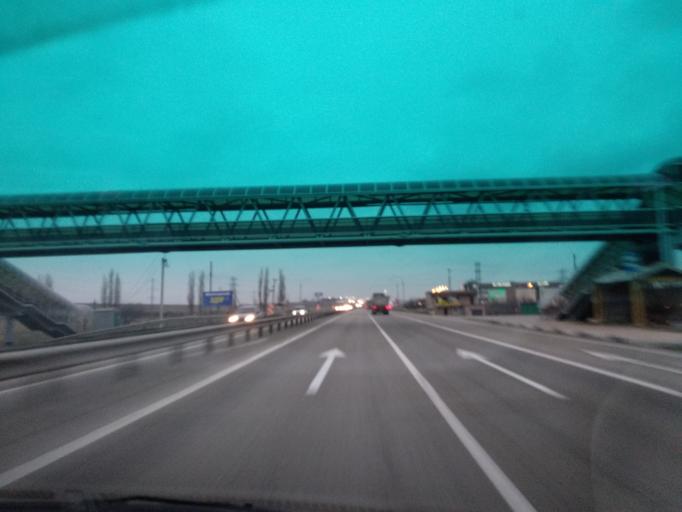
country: RU
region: Adygeya
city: Adygeysk
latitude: 44.9133
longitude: 39.1511
